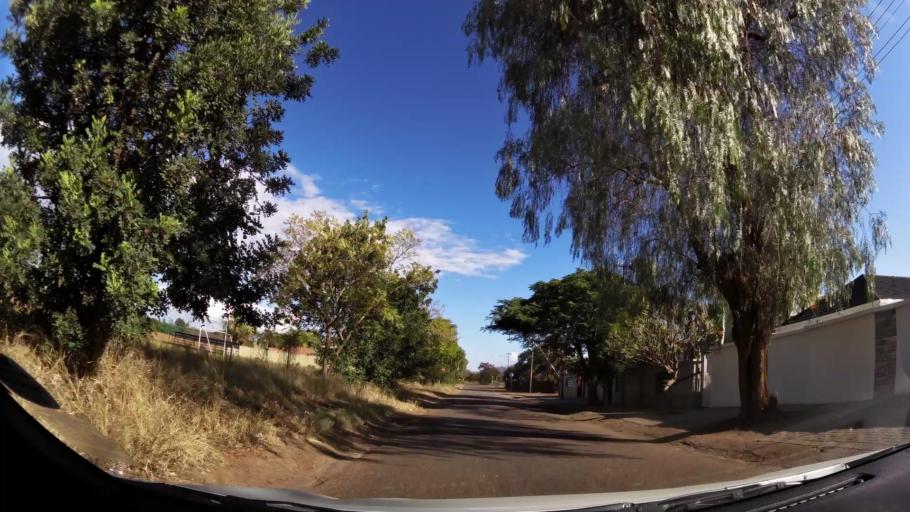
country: ZA
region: Limpopo
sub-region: Waterberg District Municipality
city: Mokopane
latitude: -24.1795
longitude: 28.9976
